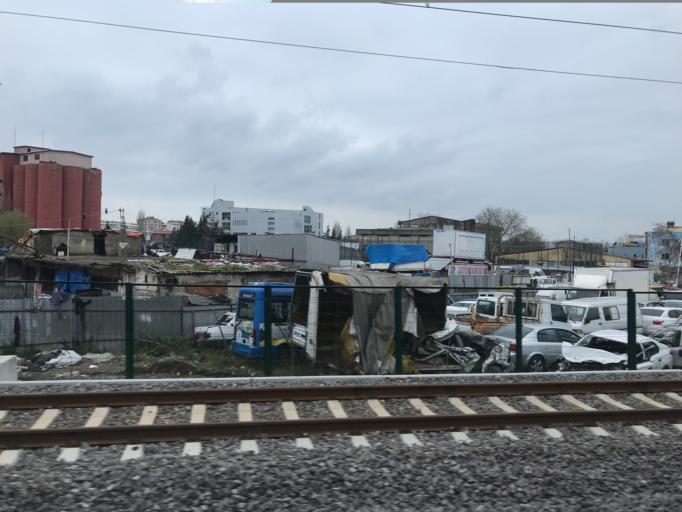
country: TR
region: Istanbul
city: Maltepe
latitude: 40.9173
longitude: 29.1414
